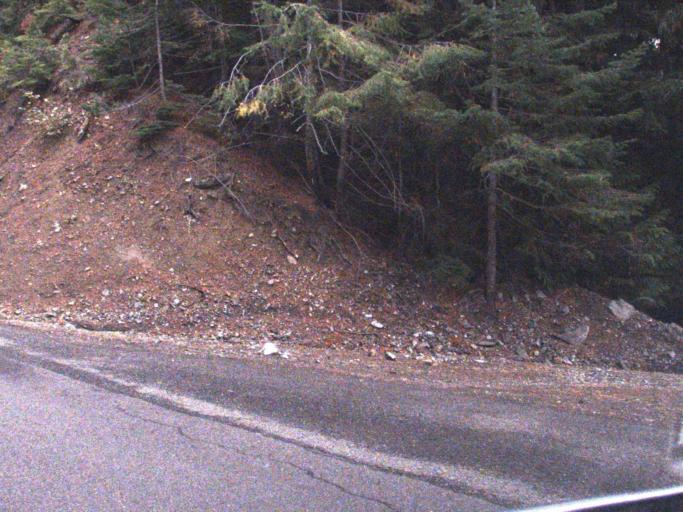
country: US
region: Washington
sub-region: Yakima County
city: Tieton
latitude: 46.6364
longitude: -121.4499
